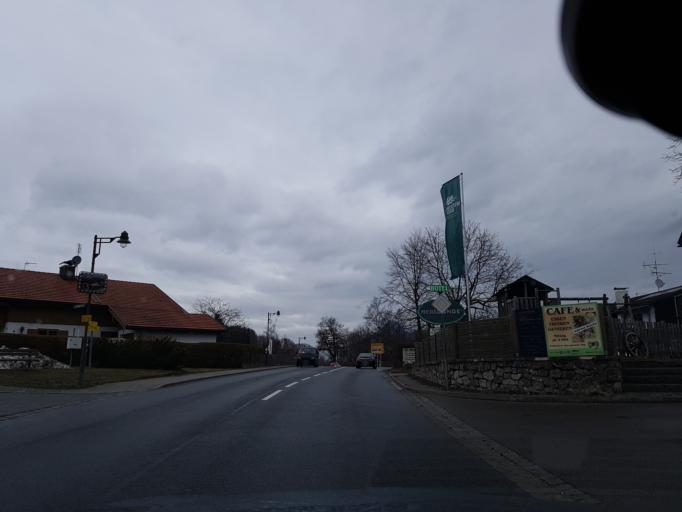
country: DE
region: Bavaria
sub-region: Upper Bavaria
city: Kiefersfelden
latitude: 47.6190
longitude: 12.1864
